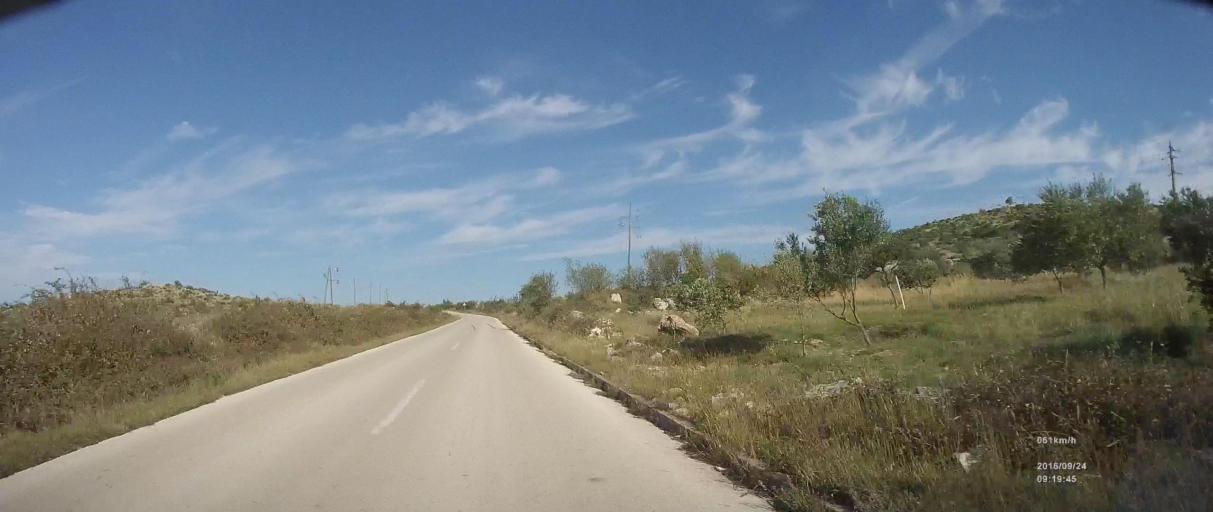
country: HR
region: Zadarska
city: Polaca
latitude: 44.0642
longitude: 15.5019
